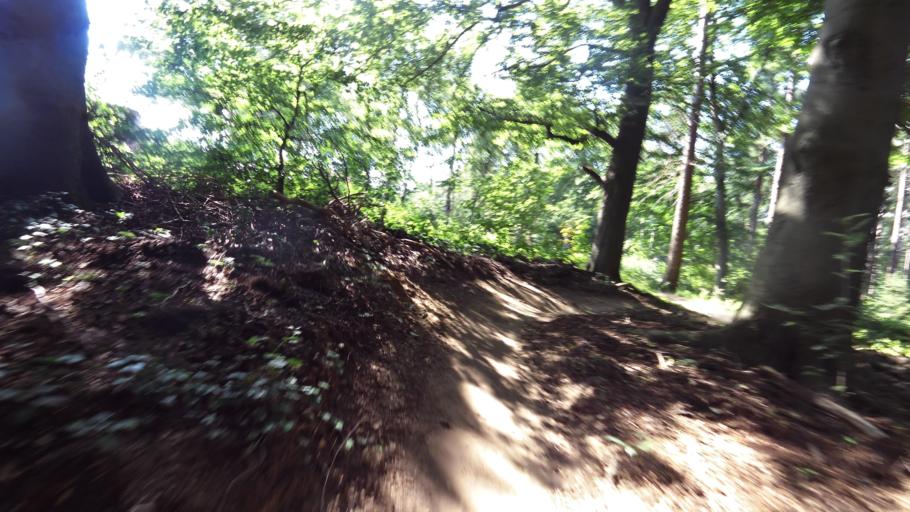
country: NL
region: Gelderland
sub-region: Gemeente Arnhem
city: Hoogkamp
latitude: 52.0086
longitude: 5.8811
